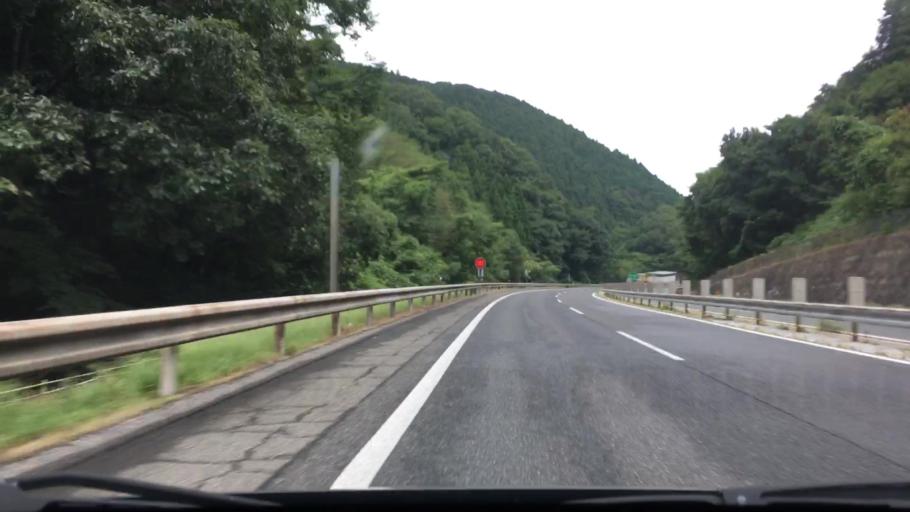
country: JP
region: Okayama
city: Niimi
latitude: 34.8946
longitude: 133.2883
